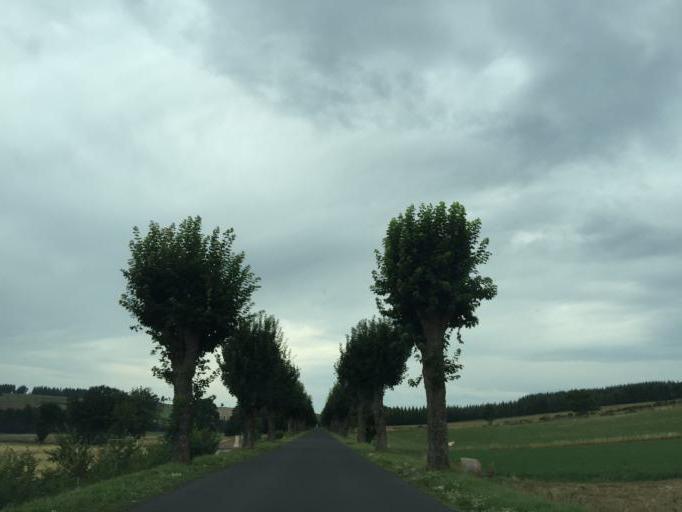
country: FR
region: Languedoc-Roussillon
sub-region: Departement de la Lozere
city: Langogne
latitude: 44.8413
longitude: 3.8217
